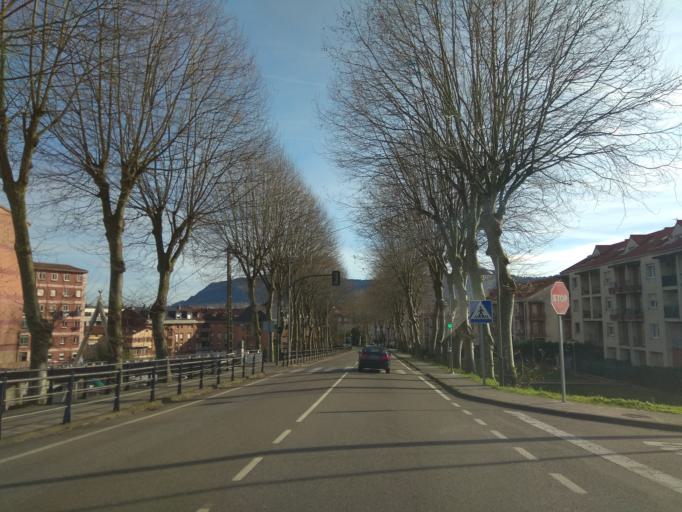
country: ES
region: Cantabria
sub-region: Provincia de Cantabria
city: El Astillero
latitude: 43.4069
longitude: -3.8414
